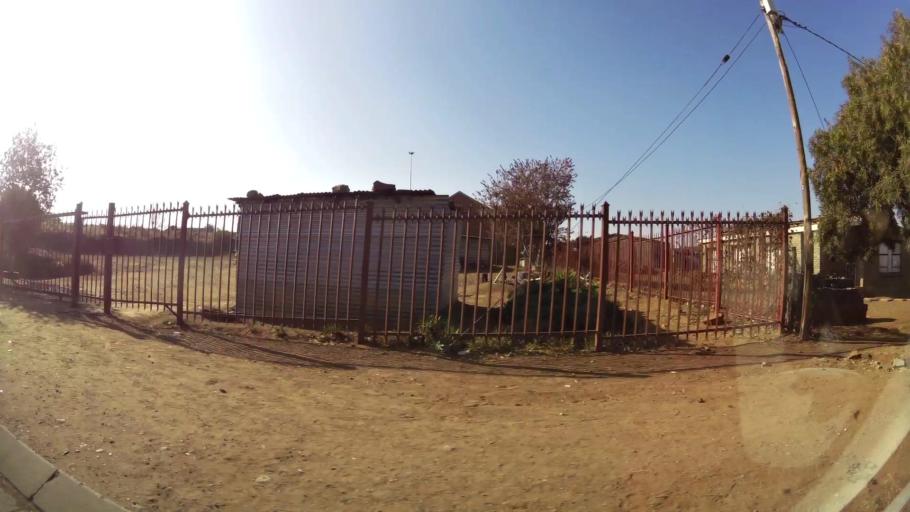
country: ZA
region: Orange Free State
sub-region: Mangaung Metropolitan Municipality
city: Bloemfontein
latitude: -29.1781
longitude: 26.2249
